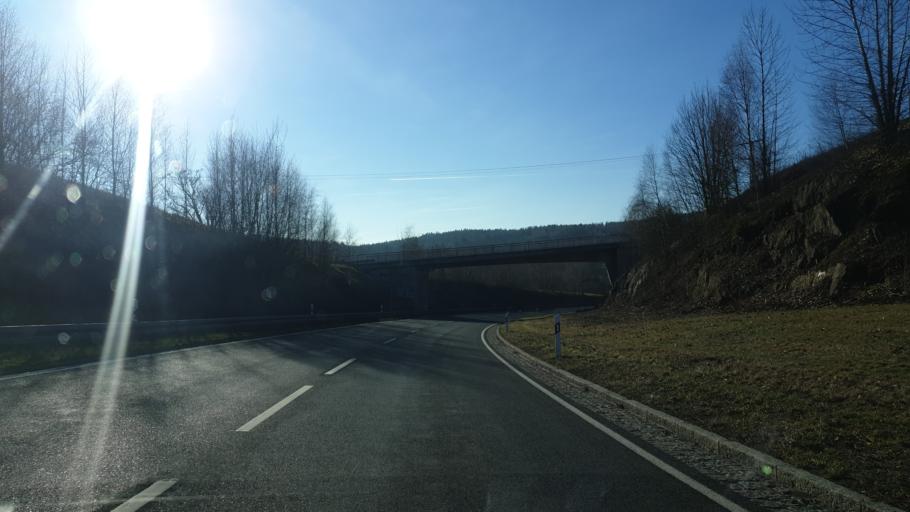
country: DE
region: Saxony
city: Bad Brambach
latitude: 50.2228
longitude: 12.3218
